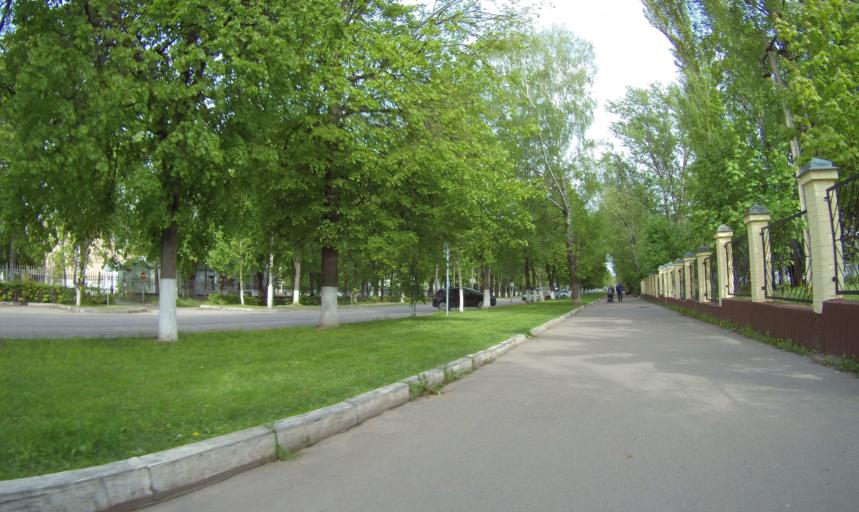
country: RU
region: Moskovskaya
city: Kolomna
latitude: 55.0895
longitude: 38.7736
